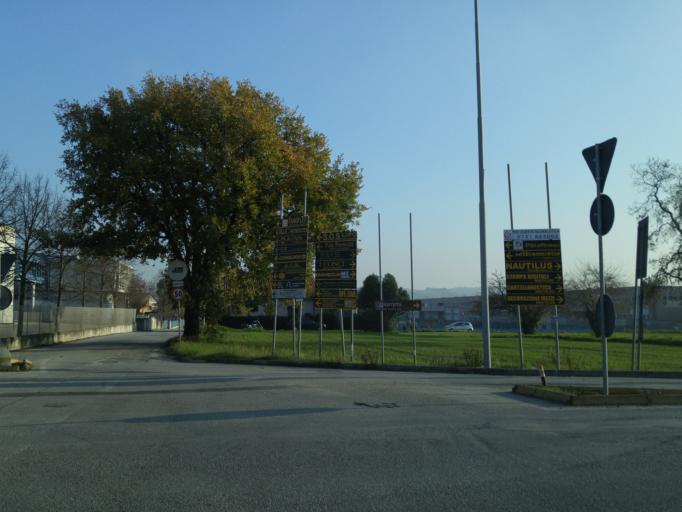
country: IT
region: The Marches
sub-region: Provincia di Pesaro e Urbino
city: Bellocchi
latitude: 43.7935
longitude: 13.0034
